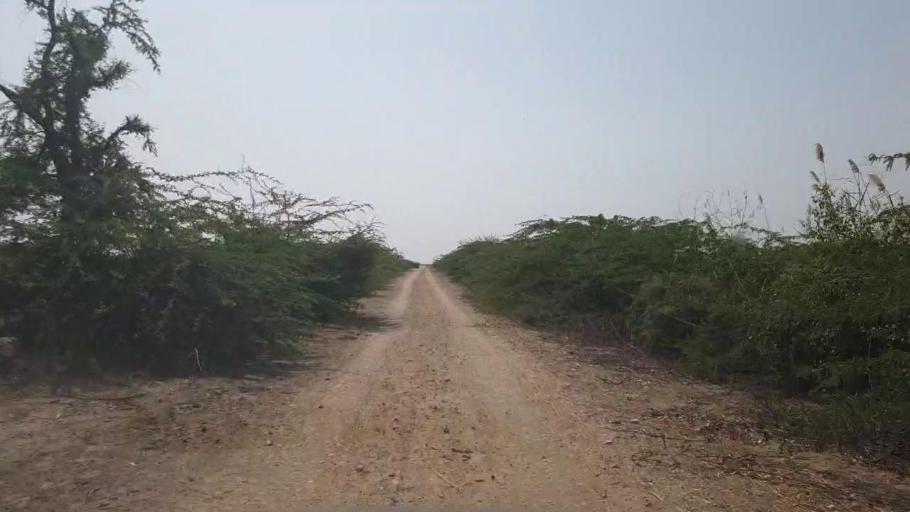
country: PK
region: Sindh
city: Jati
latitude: 24.3781
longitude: 68.6020
